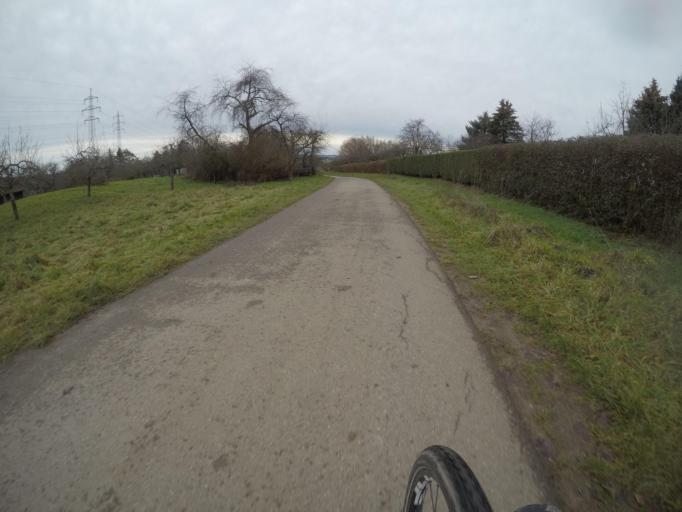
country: DE
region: Baden-Wuerttemberg
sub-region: Regierungsbezirk Stuttgart
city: Waiblingen
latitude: 48.8450
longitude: 9.3354
